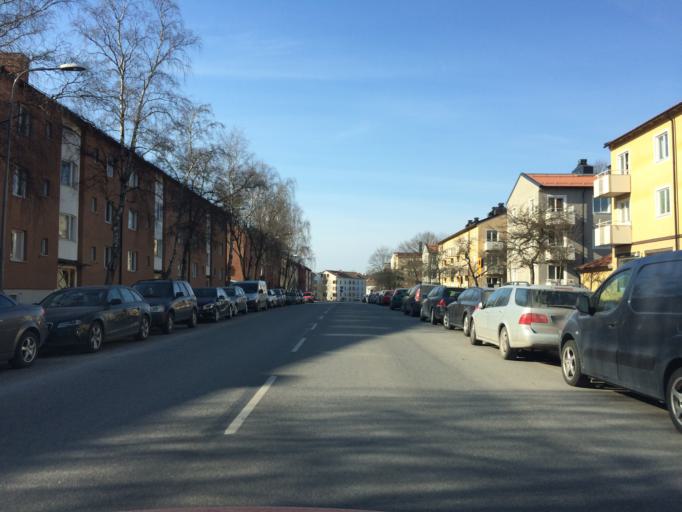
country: SE
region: Stockholm
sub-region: Stockholms Kommun
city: Arsta
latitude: 59.2992
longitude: 18.0444
